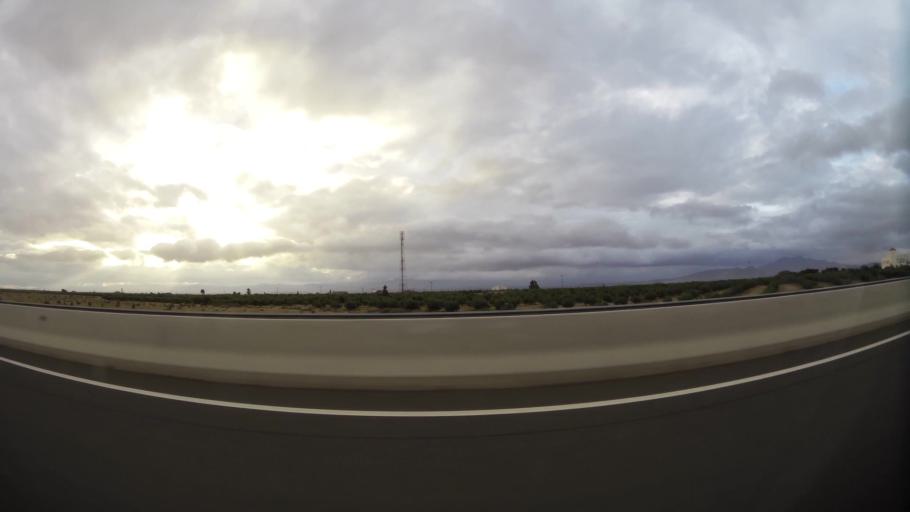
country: MA
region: Taza-Al Hoceima-Taounate
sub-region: Taza
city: Guercif
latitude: 34.3526
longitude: -3.3094
